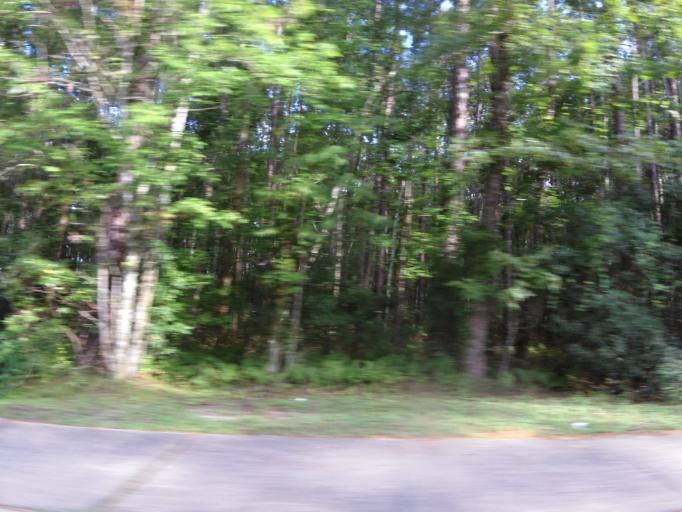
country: US
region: Florida
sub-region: Saint Johns County
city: Fruit Cove
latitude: 30.1896
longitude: -81.5897
